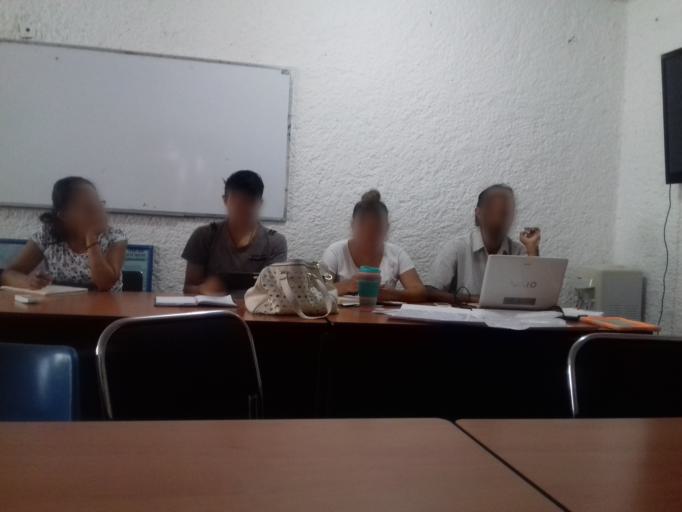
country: MX
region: Guerrero
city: Chilpancingo de los Bravos
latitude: 17.5549
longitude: -99.4979
